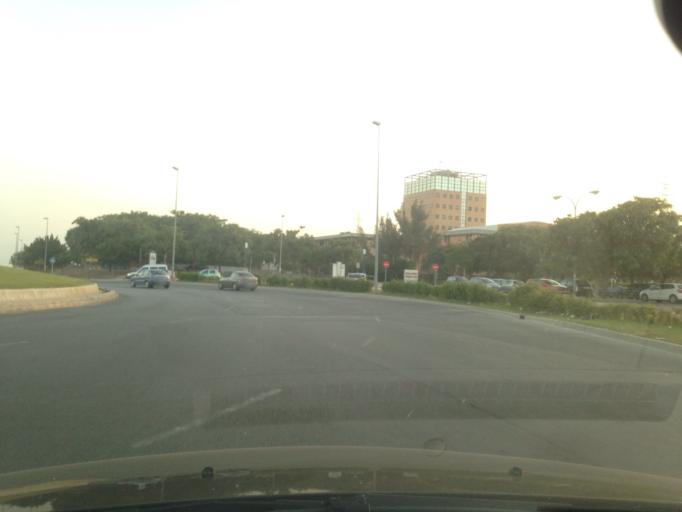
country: ES
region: Andalusia
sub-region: Provincia de Malaga
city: Malaga
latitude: 36.7178
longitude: -4.4679
